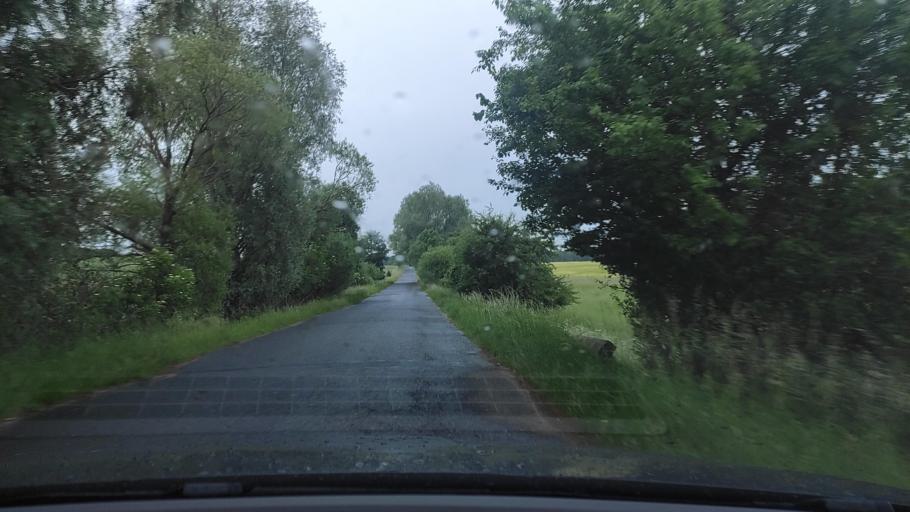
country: PL
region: Greater Poland Voivodeship
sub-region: Powiat poznanski
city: Kobylnica
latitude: 52.4930
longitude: 17.1306
